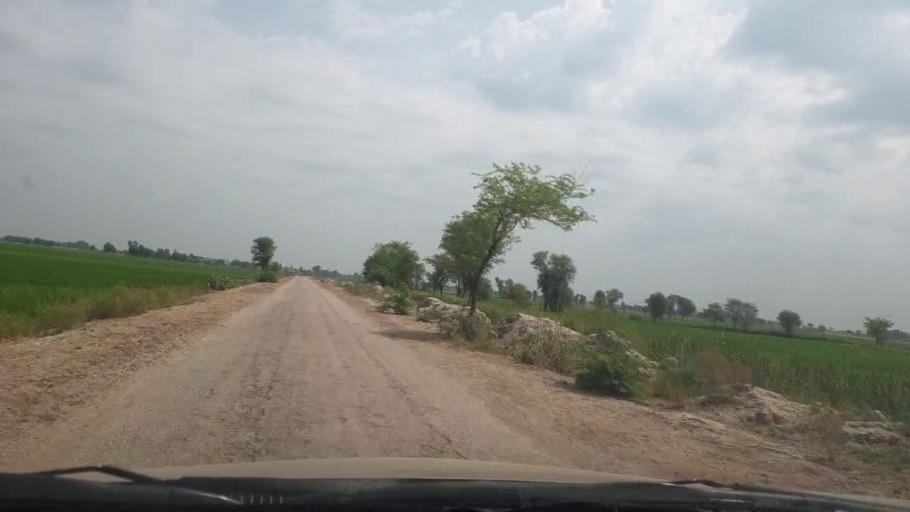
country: PK
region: Sindh
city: Miro Khan
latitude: 27.6955
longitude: 68.1994
